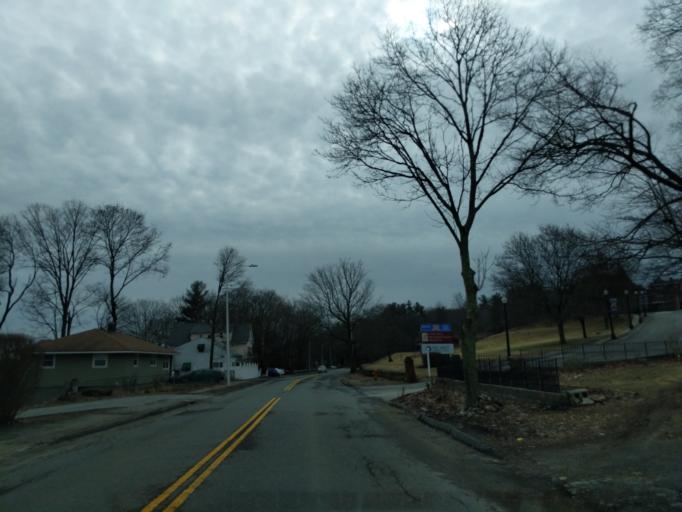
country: US
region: Massachusetts
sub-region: Worcester County
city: Worcester
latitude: 42.2623
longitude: -71.8354
